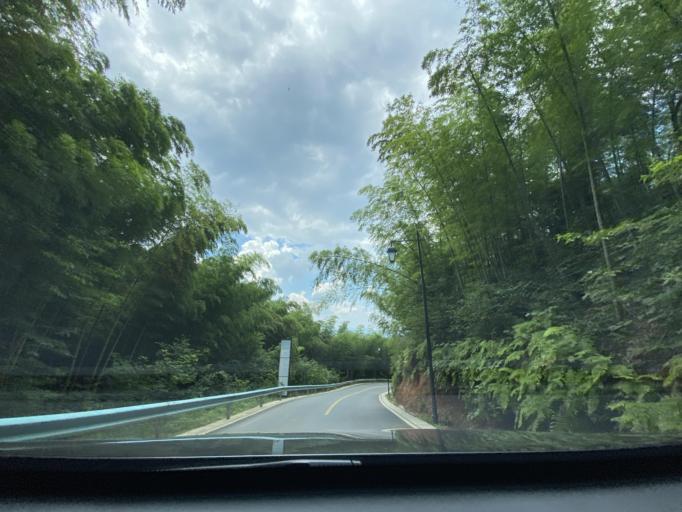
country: CN
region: Guizhou Sheng
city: Changqi
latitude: 28.5351
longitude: 105.9675
